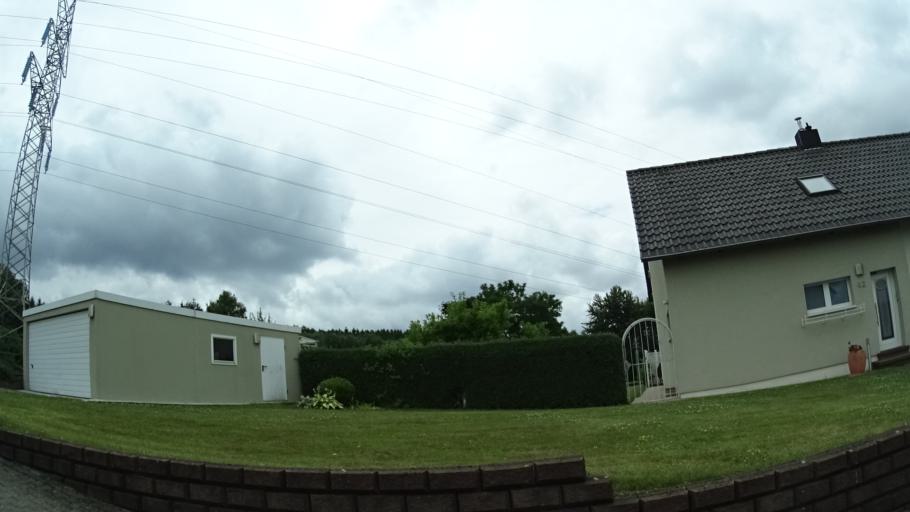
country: DE
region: Saarland
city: Merchweiler
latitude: 49.3393
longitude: 7.0058
